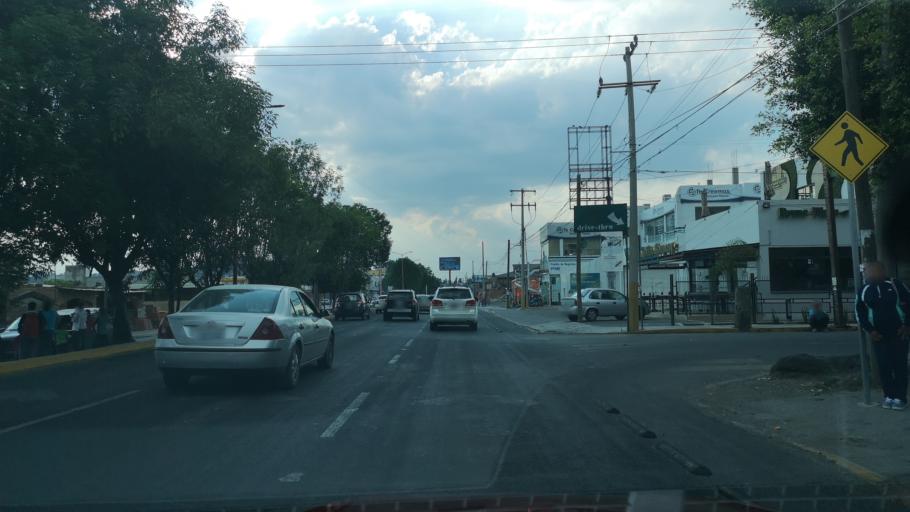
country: MX
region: Puebla
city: Cholula
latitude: 19.0702
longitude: -98.3122
